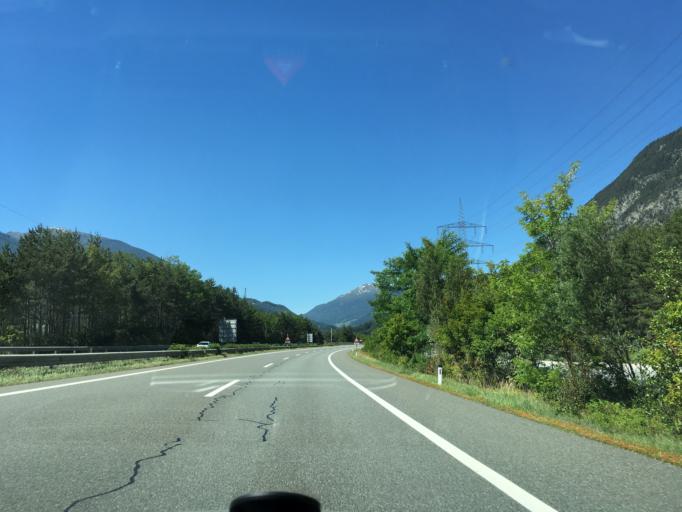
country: AT
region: Tyrol
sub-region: Politischer Bezirk Imst
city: Roppen
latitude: 47.2319
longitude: 10.8330
